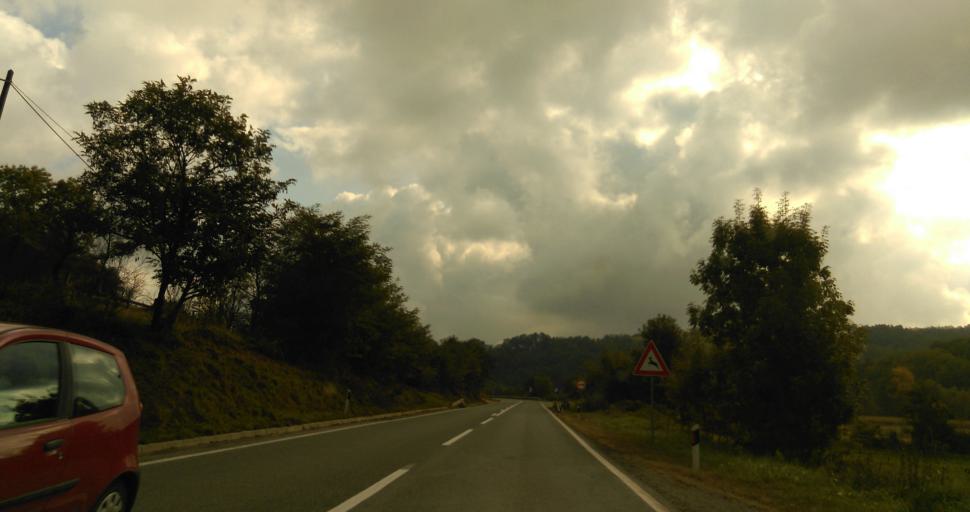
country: RS
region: Central Serbia
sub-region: Kolubarski Okrug
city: Ljig
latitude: 44.1958
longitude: 20.2912
